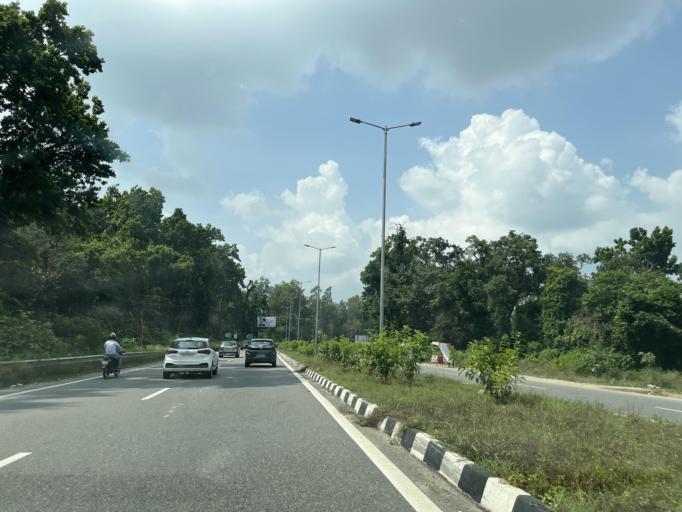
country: IN
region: Uttarakhand
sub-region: Dehradun
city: Raipur
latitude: 30.2493
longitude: 78.0946
